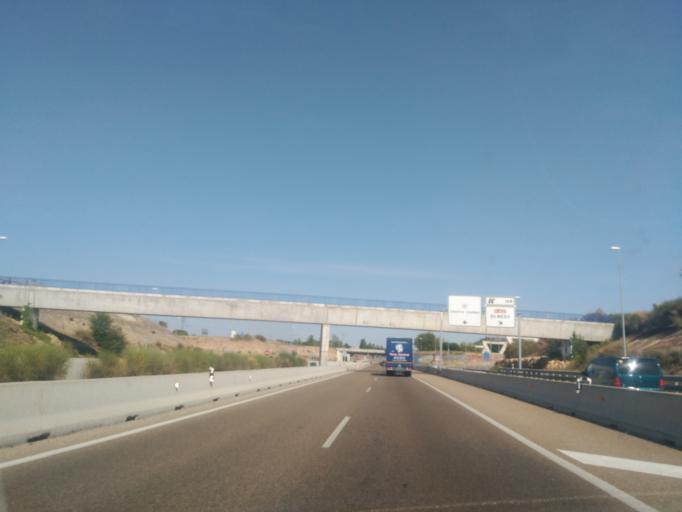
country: ES
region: Castille and Leon
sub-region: Provincia de Valladolid
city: Laguna de Duero
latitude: 41.6078
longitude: -4.7296
